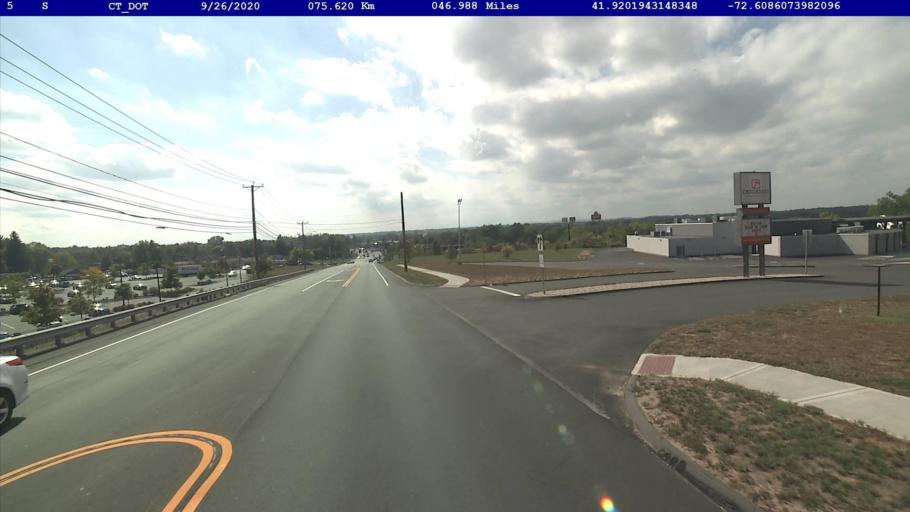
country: US
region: Connecticut
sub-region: Hartford County
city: Windsor Locks
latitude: 41.9202
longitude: -72.6086
